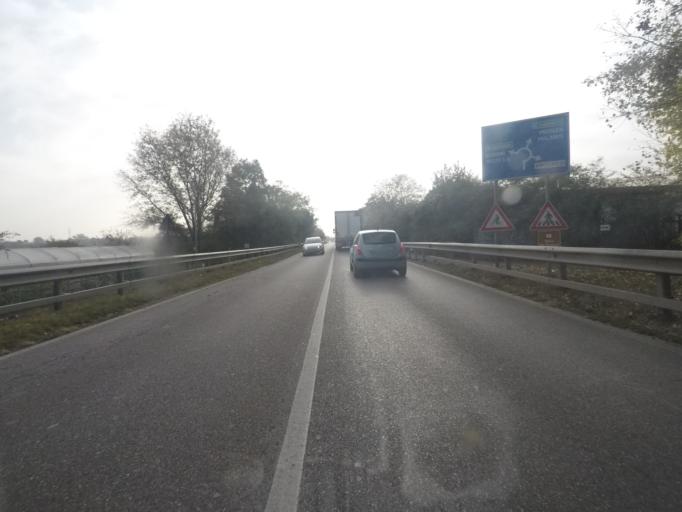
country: IT
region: Lombardy
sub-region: Provincia di Monza e Brianza
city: Vimercate
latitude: 45.6176
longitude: 9.3839
